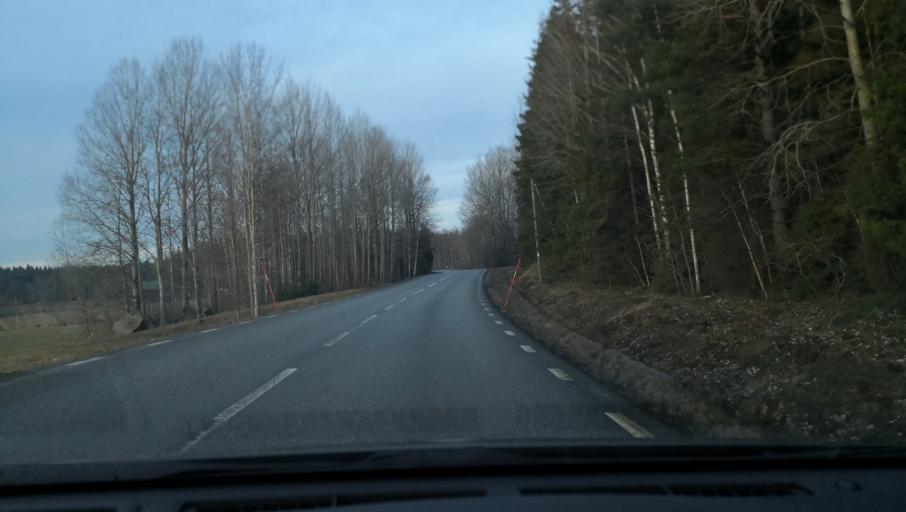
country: SE
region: OErebro
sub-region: Degerfors Kommun
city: Degerfors
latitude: 59.1304
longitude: 14.4096
